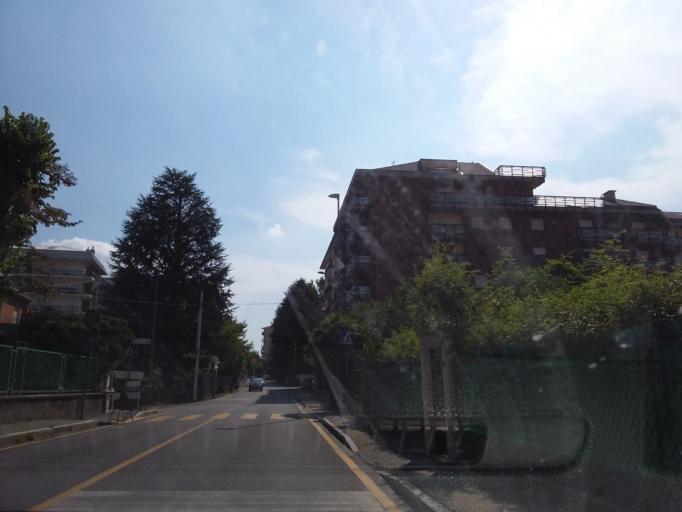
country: IT
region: Piedmont
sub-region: Provincia di Torino
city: Rivoli
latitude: 45.0741
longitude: 7.5406
